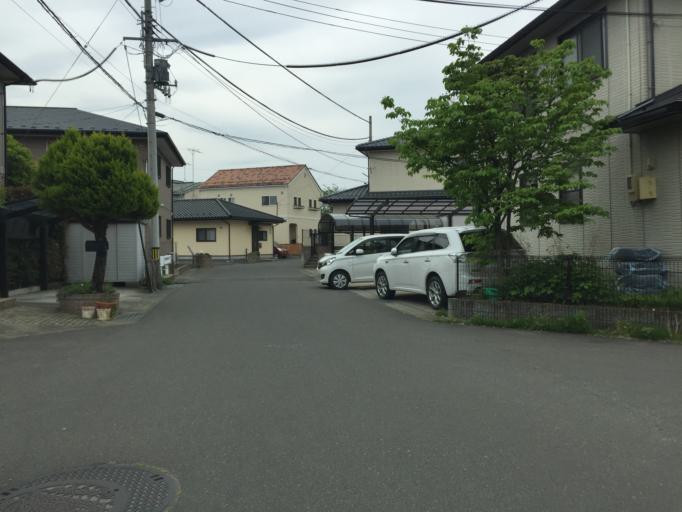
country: JP
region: Fukushima
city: Fukushima-shi
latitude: 37.7844
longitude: 140.4486
